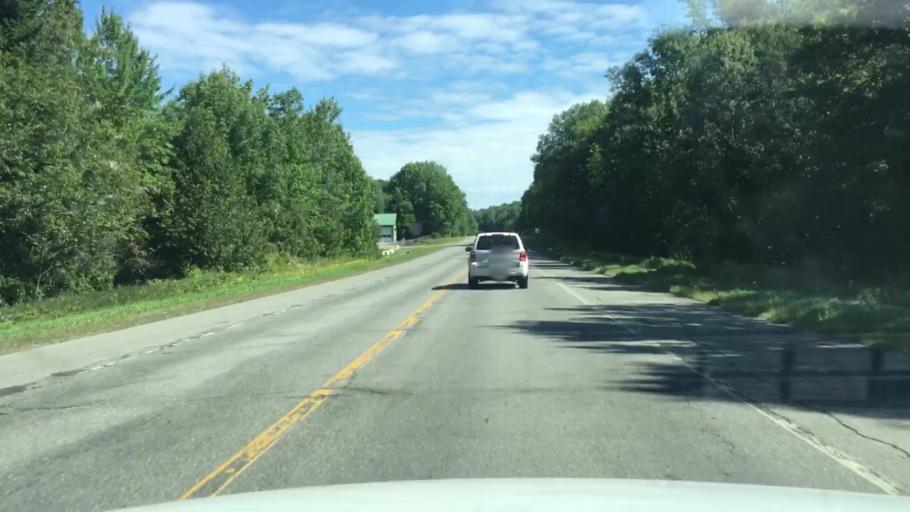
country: US
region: Maine
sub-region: Penobscot County
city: Dexter
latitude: 45.0486
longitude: -69.2677
